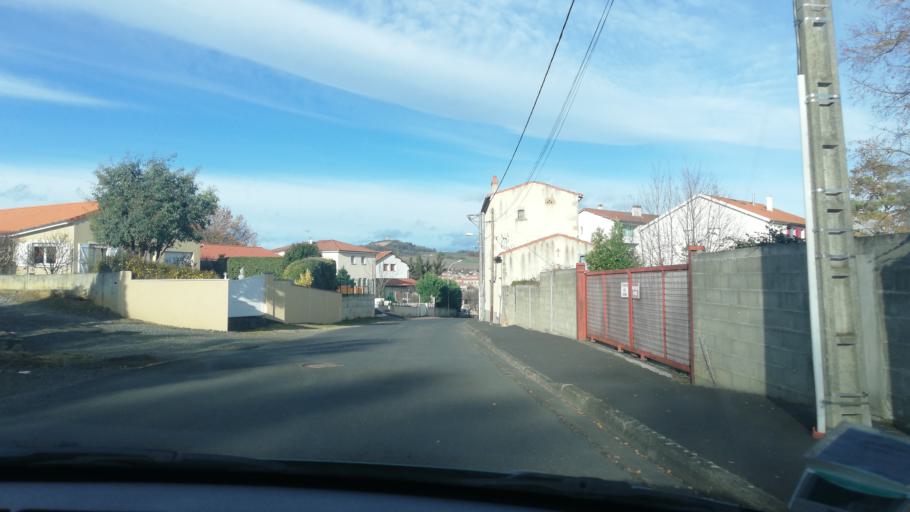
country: FR
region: Auvergne
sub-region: Departement du Puy-de-Dome
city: Billom
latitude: 45.7178
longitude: 3.3416
